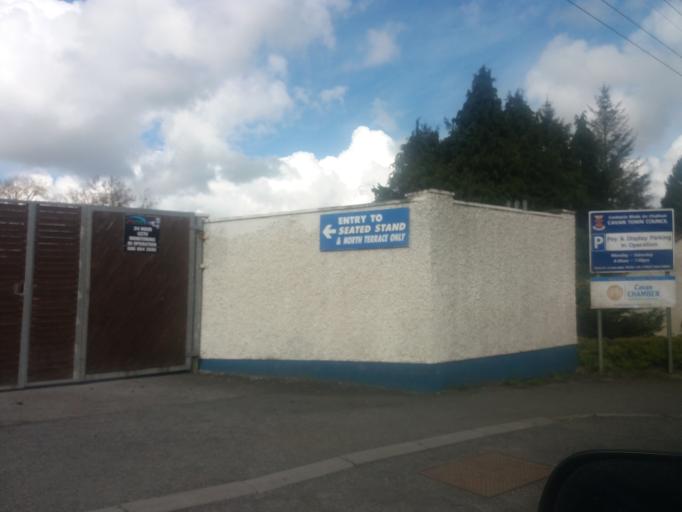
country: IE
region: Ulster
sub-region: An Cabhan
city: Cavan
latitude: 53.9843
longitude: -7.3589
